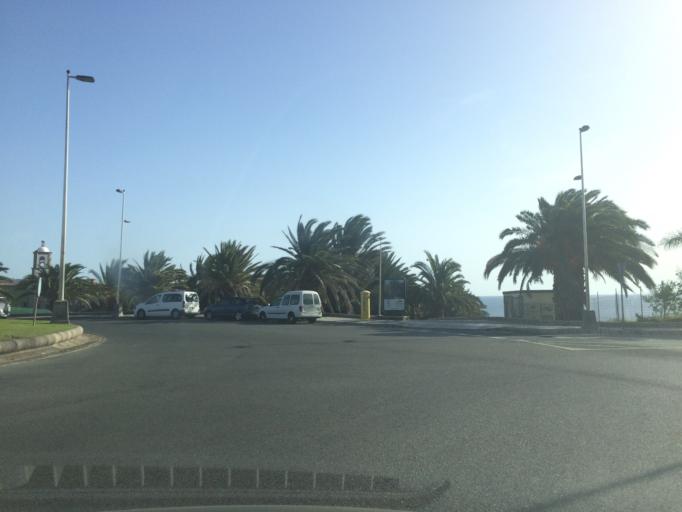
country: ES
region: Canary Islands
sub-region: Provincia de Las Palmas
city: Maspalomas
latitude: 27.7446
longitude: -15.6078
